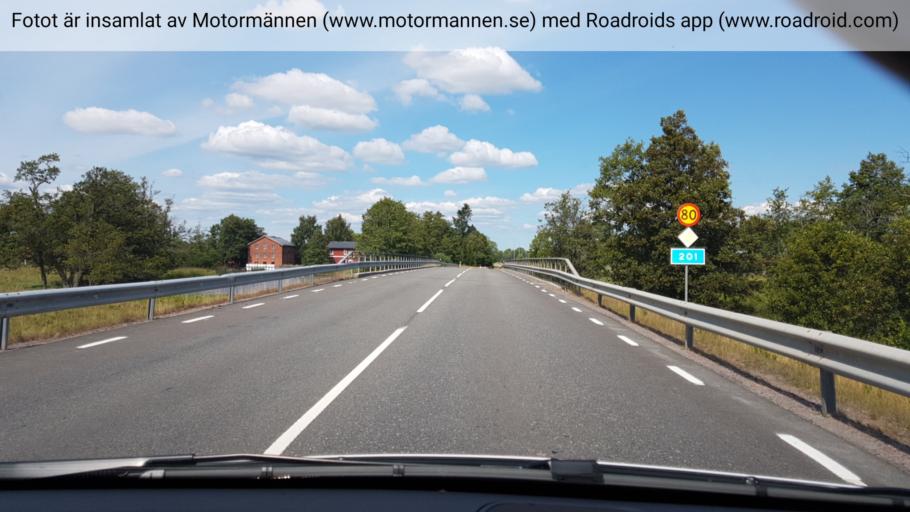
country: SE
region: Vaestra Goetaland
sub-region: Toreboda Kommun
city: Toereboda
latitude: 58.5755
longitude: 14.0964
